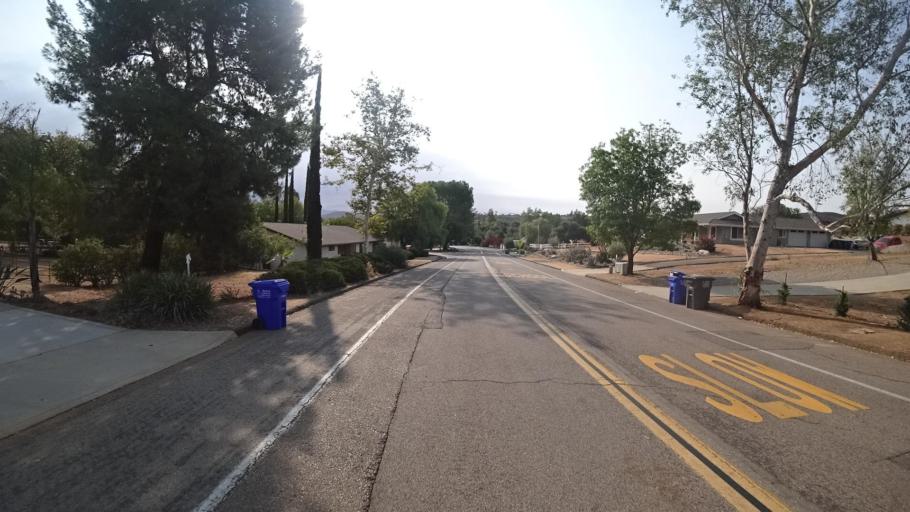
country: US
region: California
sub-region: San Diego County
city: San Diego Country Estates
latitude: 33.0085
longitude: -116.7963
